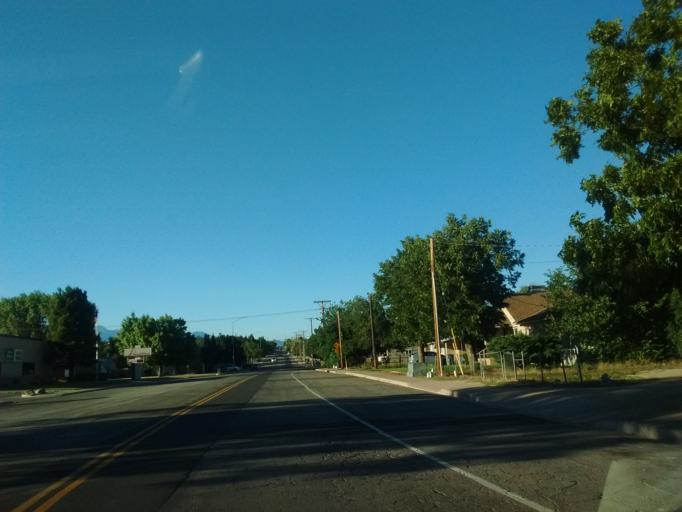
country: US
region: Utah
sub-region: Washington County
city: Hurricane
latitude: 37.1772
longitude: -113.2918
